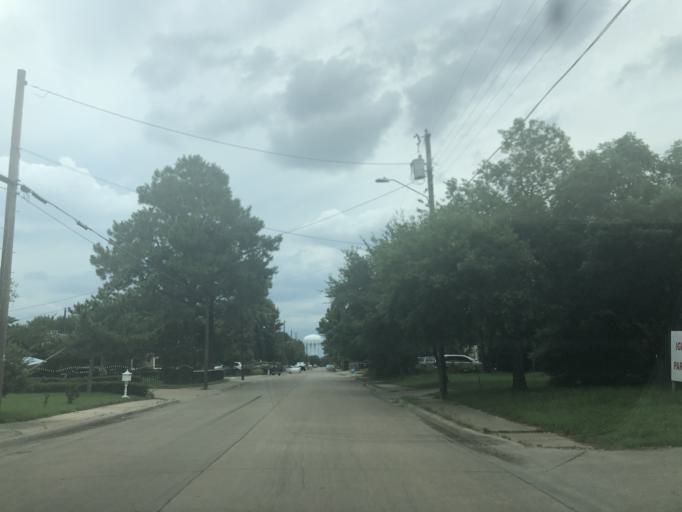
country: US
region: Texas
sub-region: Dallas County
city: Irving
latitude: 32.8054
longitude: -96.9299
